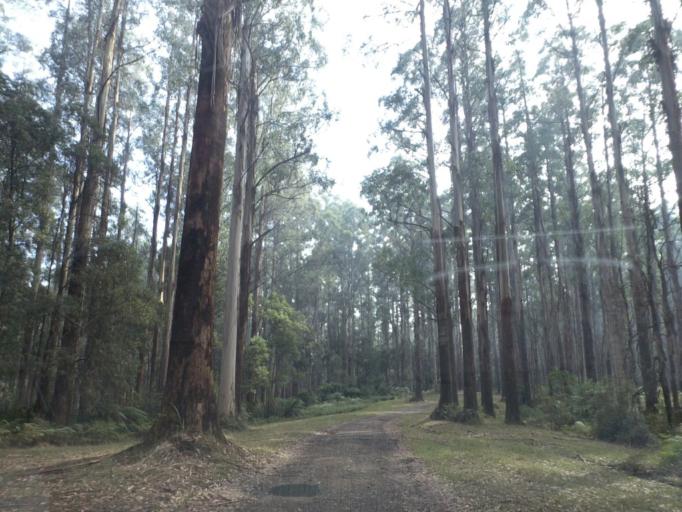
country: AU
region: Victoria
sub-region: Yarra Ranges
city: Healesville
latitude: -37.5710
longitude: 145.5825
